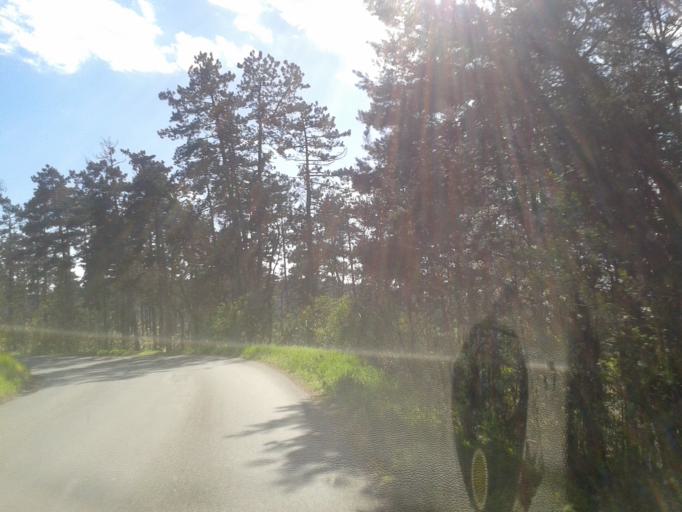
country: CZ
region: Central Bohemia
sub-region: Okres Beroun
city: Beroun
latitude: 49.9283
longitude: 14.0716
